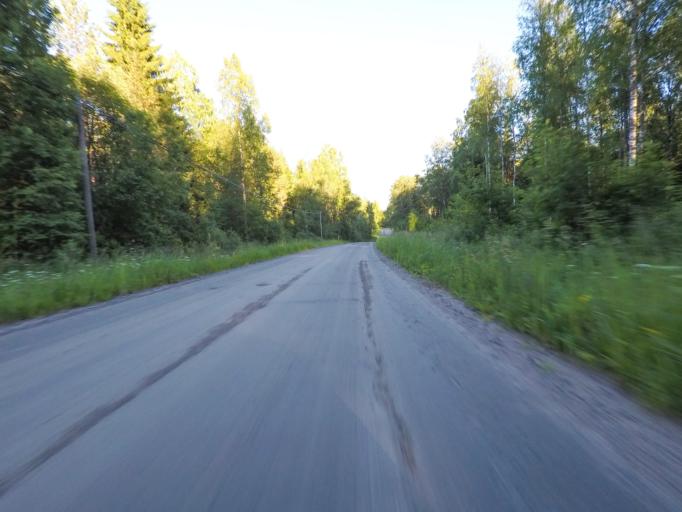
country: FI
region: Northern Savo
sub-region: Kuopio
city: Maaninka
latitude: 62.8751
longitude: 27.3052
